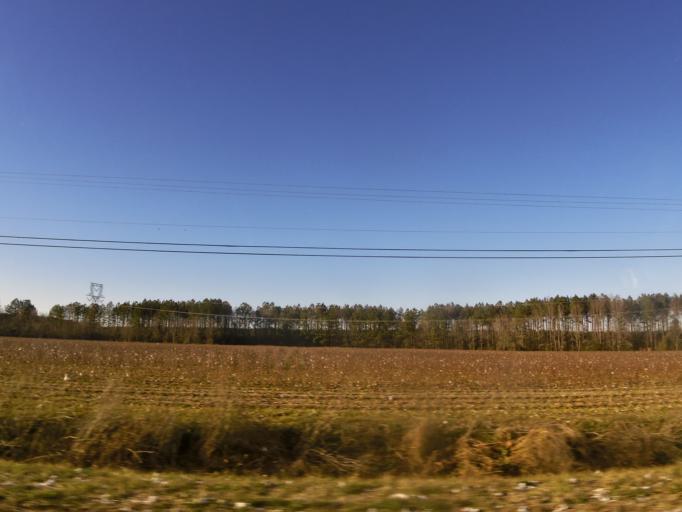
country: US
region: Virginia
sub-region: City of Franklin
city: Franklin
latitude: 36.6695
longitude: -76.7963
